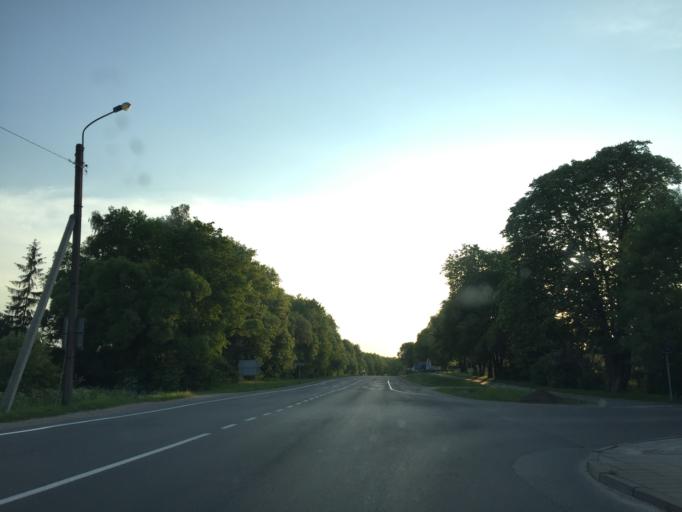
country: LT
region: Siauliu apskritis
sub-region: Siauliai
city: Siauliai
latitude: 55.9437
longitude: 23.2809
